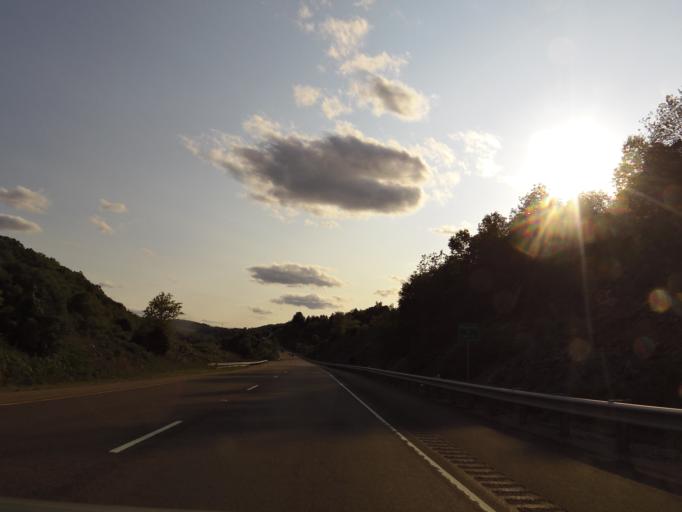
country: US
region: Virginia
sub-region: Tazewell County
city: Raven
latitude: 36.9973
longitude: -81.8295
